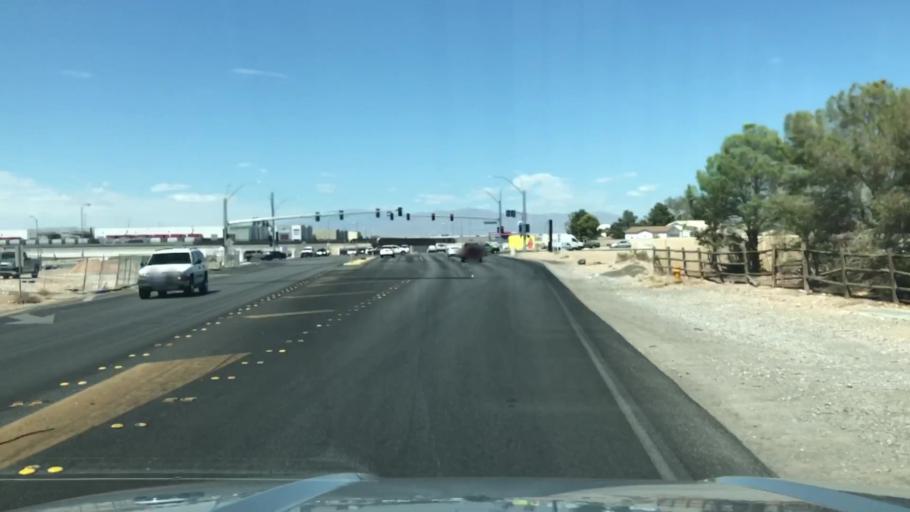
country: US
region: Nevada
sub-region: Clark County
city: Enterprise
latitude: 36.0559
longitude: -115.2078
